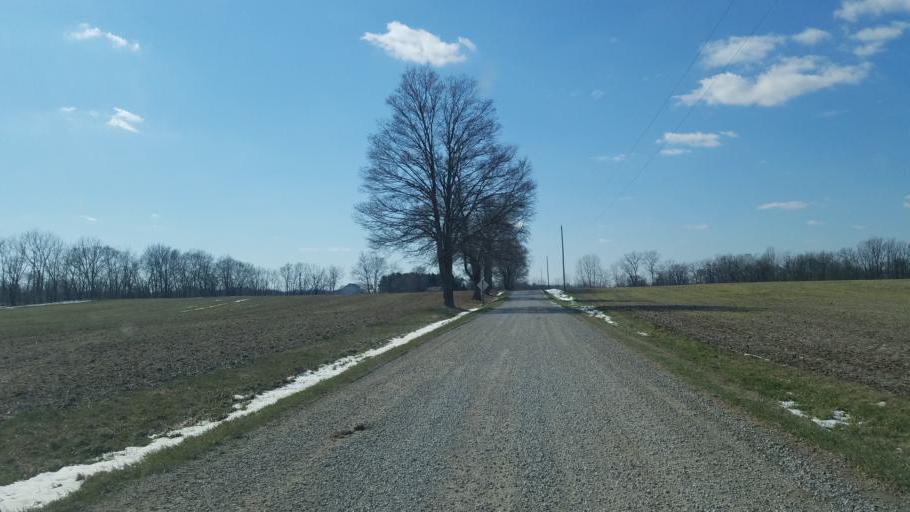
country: US
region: Ohio
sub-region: Knox County
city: Fredericktown
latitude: 40.4563
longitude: -82.6460
